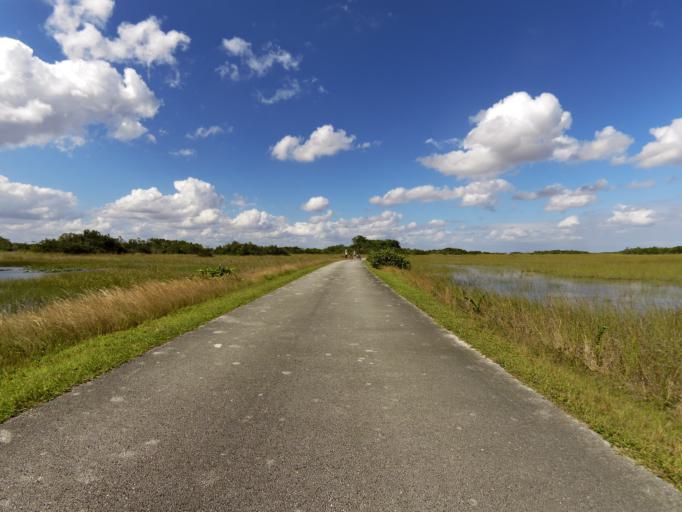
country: US
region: Florida
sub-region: Miami-Dade County
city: The Hammocks
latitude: 25.6981
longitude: -80.7629
